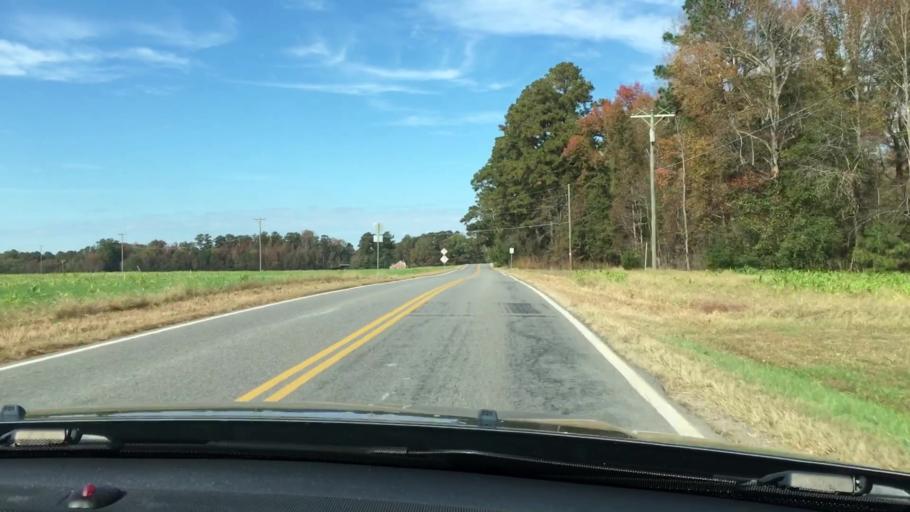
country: US
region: Virginia
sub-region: King William County
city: West Point
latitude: 37.5130
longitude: -76.8201
